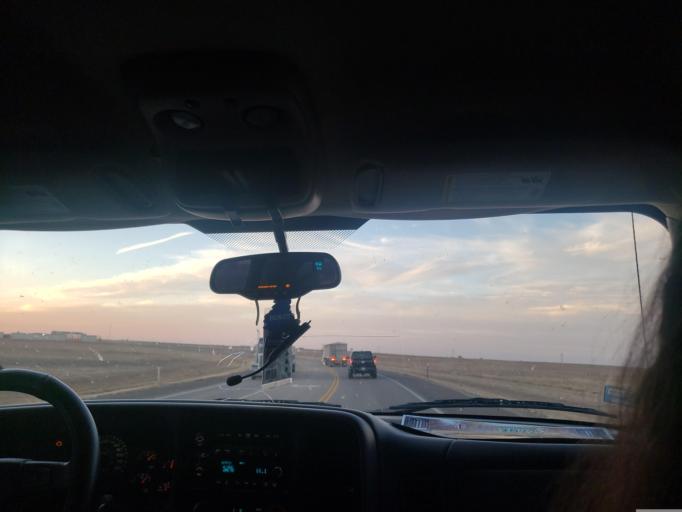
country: US
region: Kansas
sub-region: Seward County
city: Liberal
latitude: 37.0692
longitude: -100.9067
